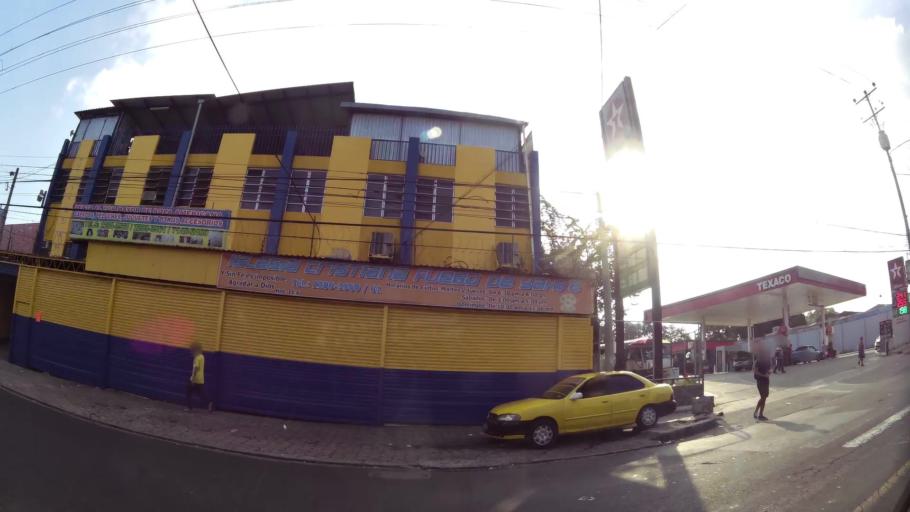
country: SV
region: San Salvador
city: San Salvador
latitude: 13.6927
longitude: -89.2190
